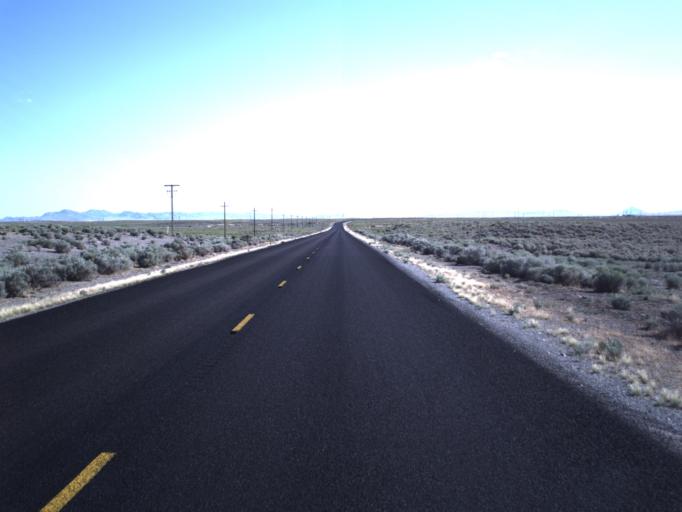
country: US
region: Utah
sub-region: Beaver County
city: Milford
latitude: 38.4471
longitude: -113.0085
